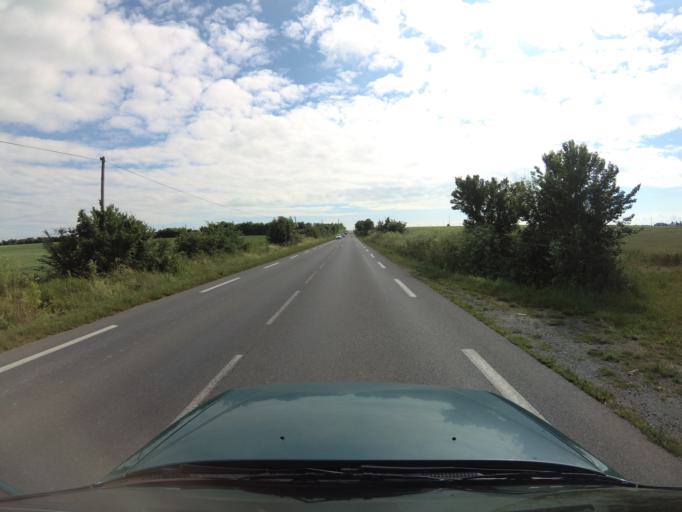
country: FR
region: Poitou-Charentes
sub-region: Departement de la Charente-Maritime
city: Saint-Xandre
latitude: 46.2291
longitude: -1.0794
